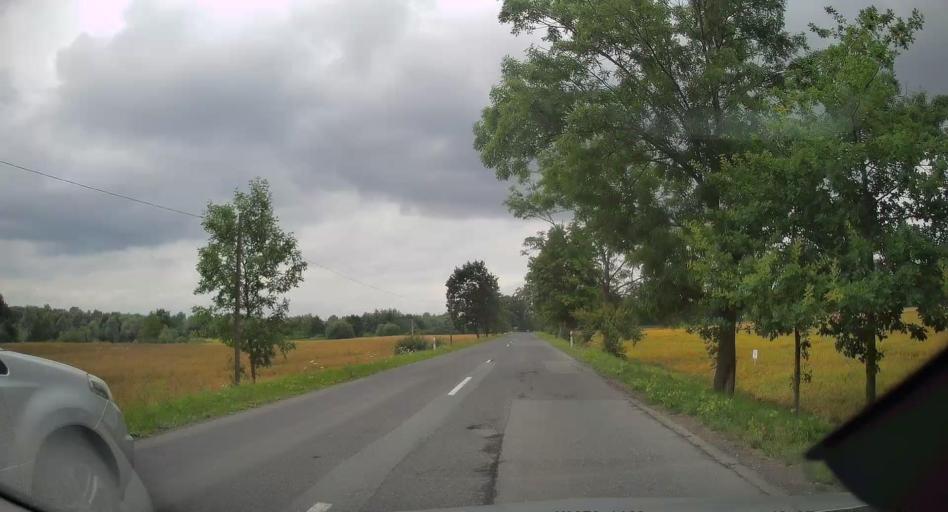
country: PL
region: Opole Voivodeship
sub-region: Powiat nyski
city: Paczkow
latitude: 50.4731
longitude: 17.0098
